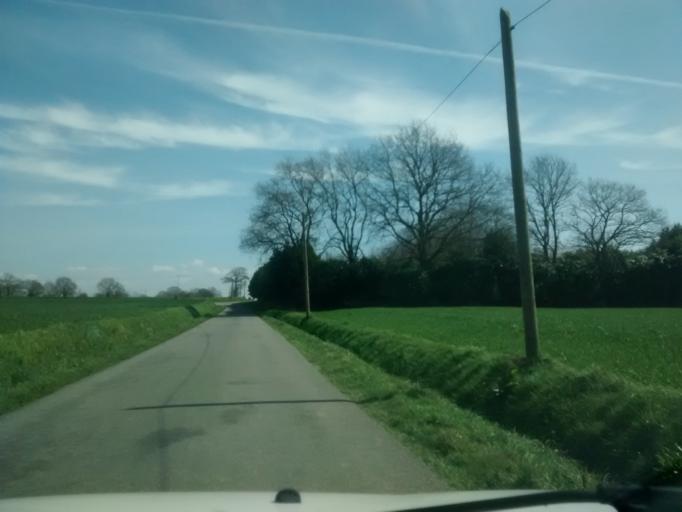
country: FR
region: Brittany
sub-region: Departement d'Ille-et-Vilaine
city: Brece
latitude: 48.0967
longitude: -1.4898
